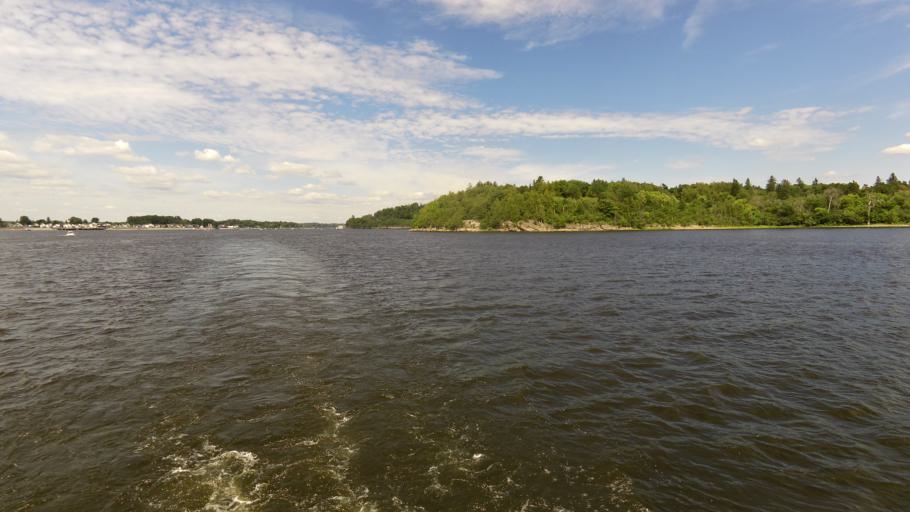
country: CA
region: Quebec
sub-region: Outaouais
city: Gatineau
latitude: 45.4468
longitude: -75.6965
